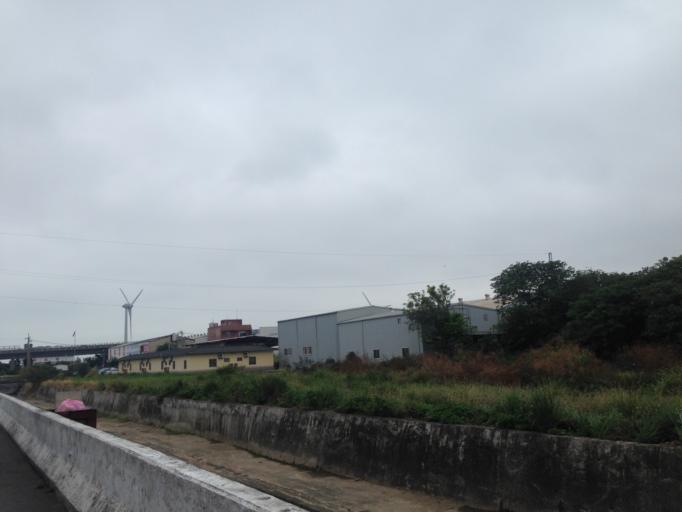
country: TW
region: Taiwan
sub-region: Miaoli
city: Miaoli
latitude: 24.6977
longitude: 120.8642
